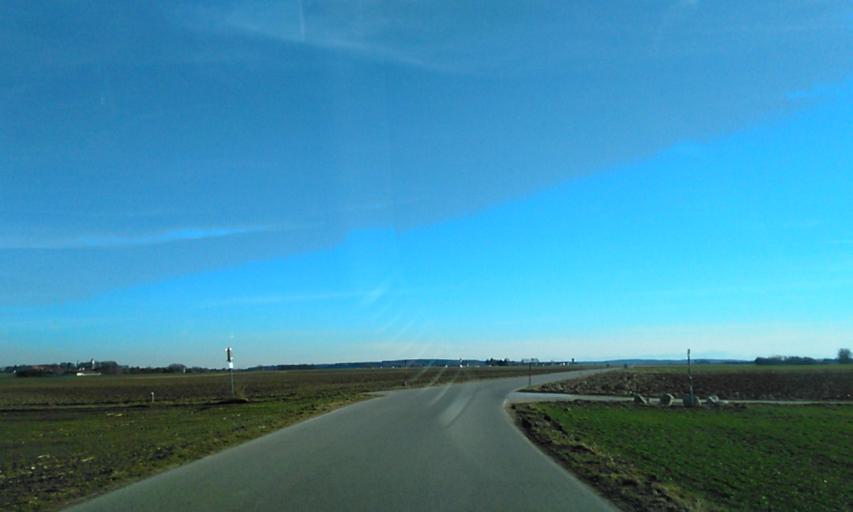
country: DE
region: Bavaria
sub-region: Swabia
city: Merching
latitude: 48.2375
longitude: 10.9920
